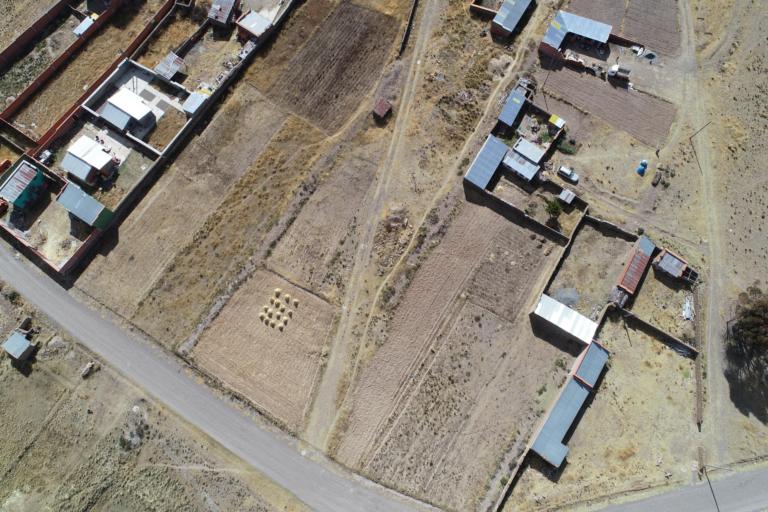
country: BO
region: La Paz
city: Achacachi
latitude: -15.8967
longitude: -68.9093
